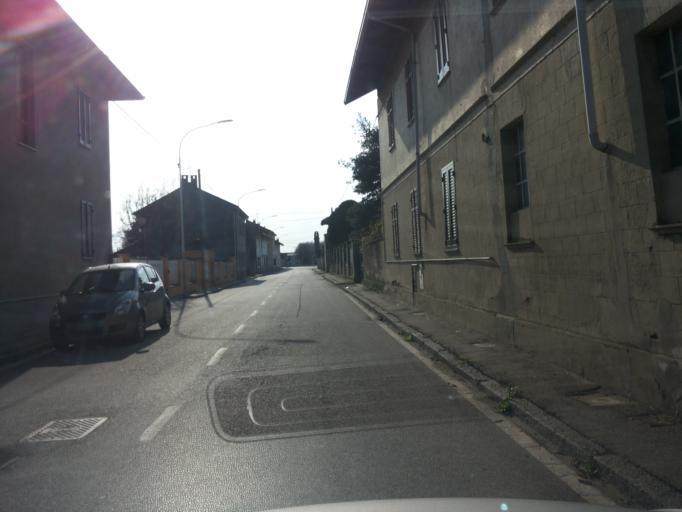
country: IT
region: Piedmont
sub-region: Provincia di Vercelli
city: Caresana
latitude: 45.2235
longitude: 8.5026
